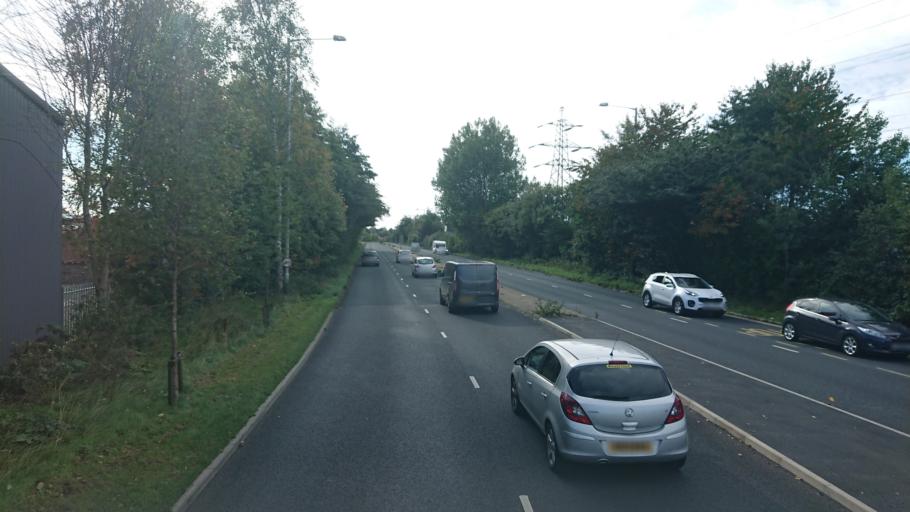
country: GB
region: England
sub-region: Lancashire
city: Morecambe
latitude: 54.0582
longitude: -2.8350
